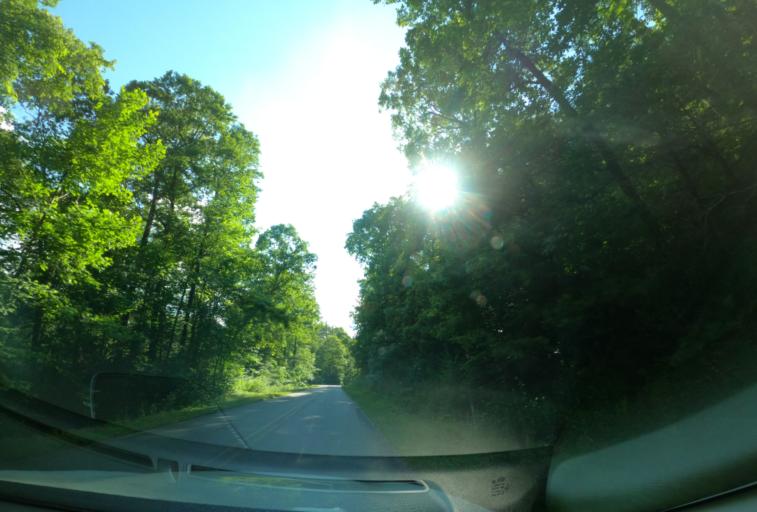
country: US
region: North Carolina
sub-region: Transylvania County
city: Brevard
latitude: 35.2854
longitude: -82.7948
